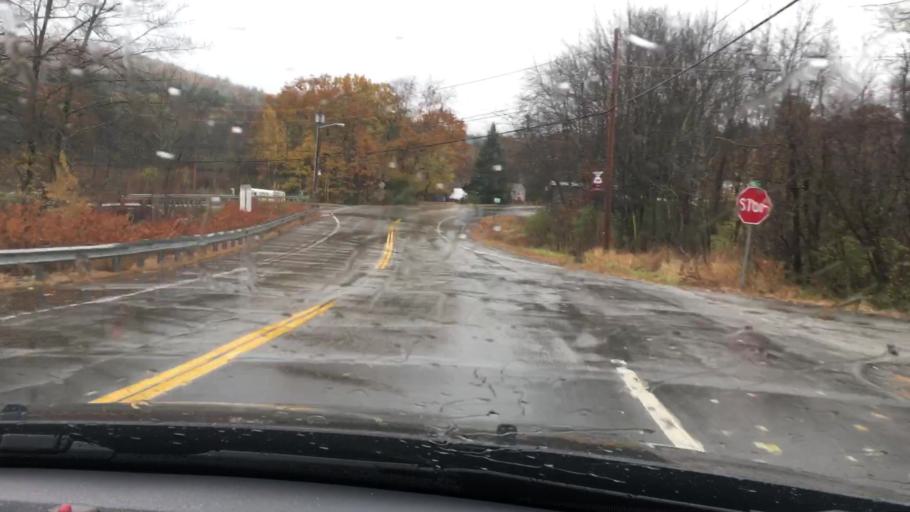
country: US
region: New Hampshire
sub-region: Grafton County
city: Ashland
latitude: 43.7048
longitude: -71.6305
